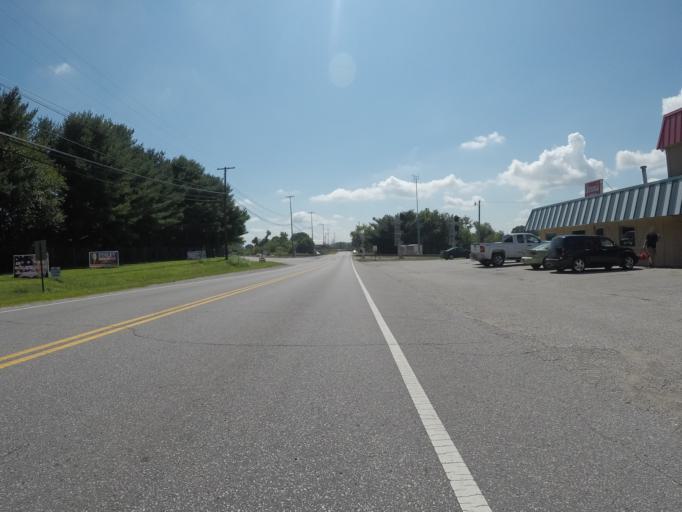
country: US
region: Ohio
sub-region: Lawrence County
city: South Point
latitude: 38.4228
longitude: -82.5901
